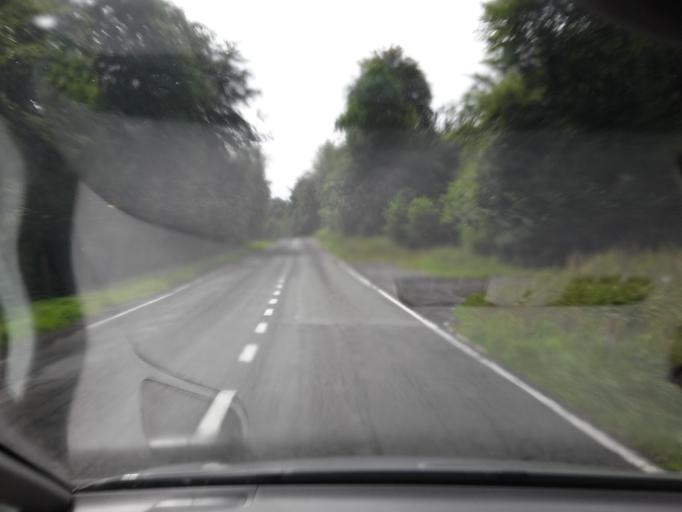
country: BE
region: Wallonia
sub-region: Province du Luxembourg
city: Chiny
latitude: 49.7772
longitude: 5.3495
